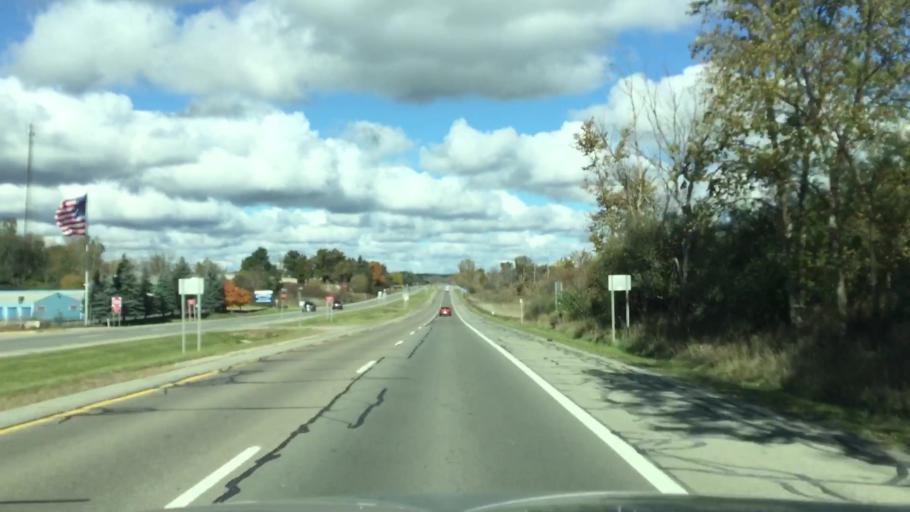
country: US
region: Michigan
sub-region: Oakland County
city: Oxford
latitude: 42.8549
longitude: -83.2847
